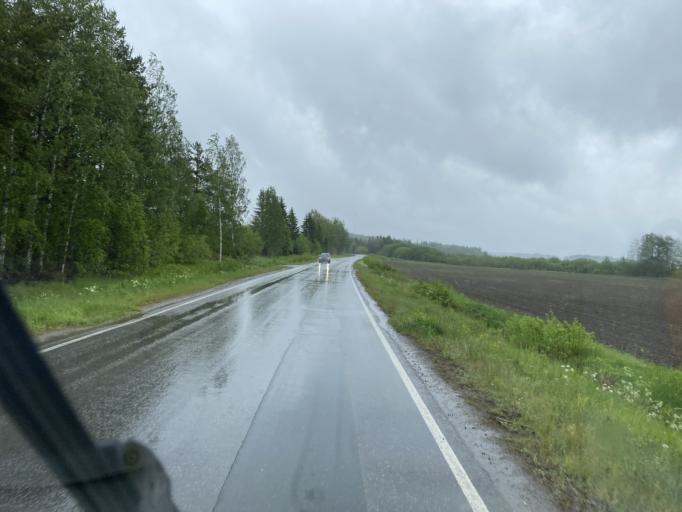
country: FI
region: Pirkanmaa
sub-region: Etelae-Pirkanmaa
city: Urjala
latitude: 61.0380
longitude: 23.4615
